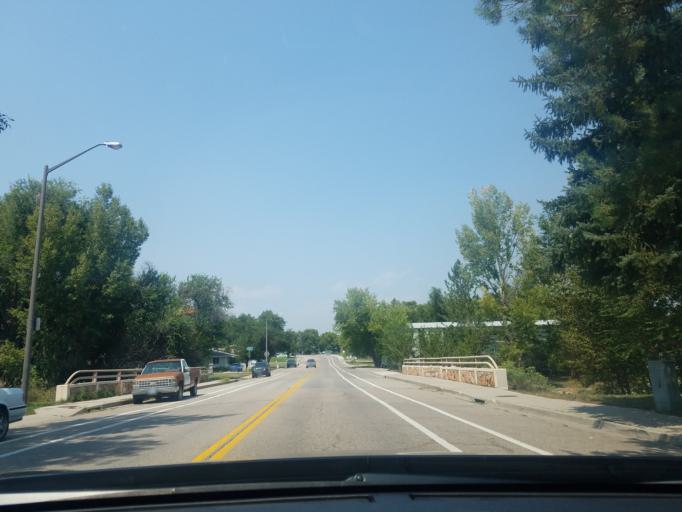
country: US
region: Colorado
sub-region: Larimer County
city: Fort Collins
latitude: 40.5638
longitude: -105.0675
